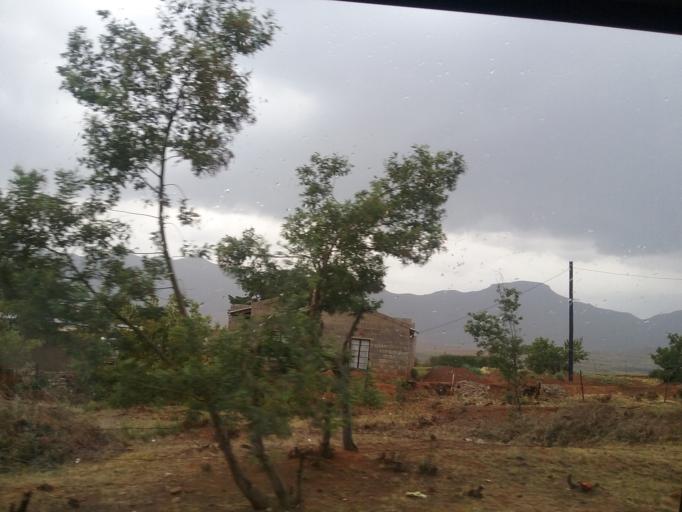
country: LS
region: Maseru
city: Nako
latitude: -29.4876
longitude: 27.7488
